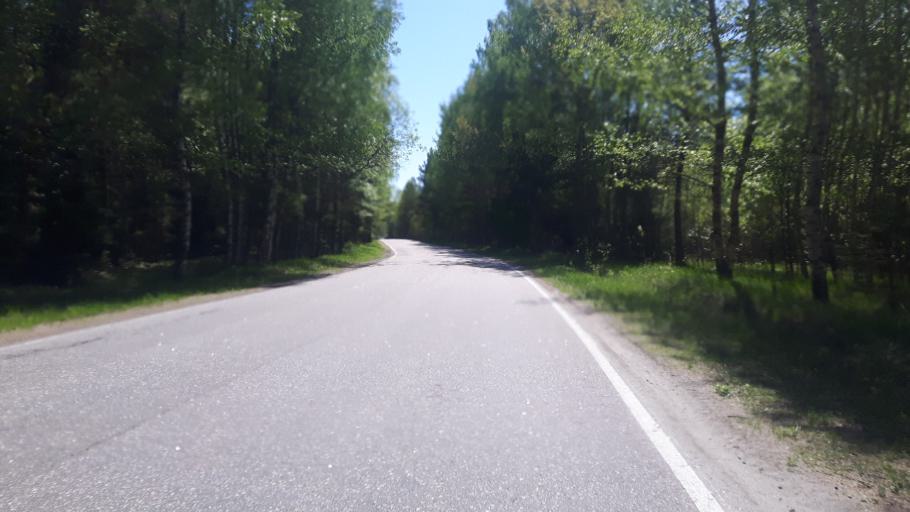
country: RU
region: Leningrad
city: Glebychevo
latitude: 60.3439
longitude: 28.8222
